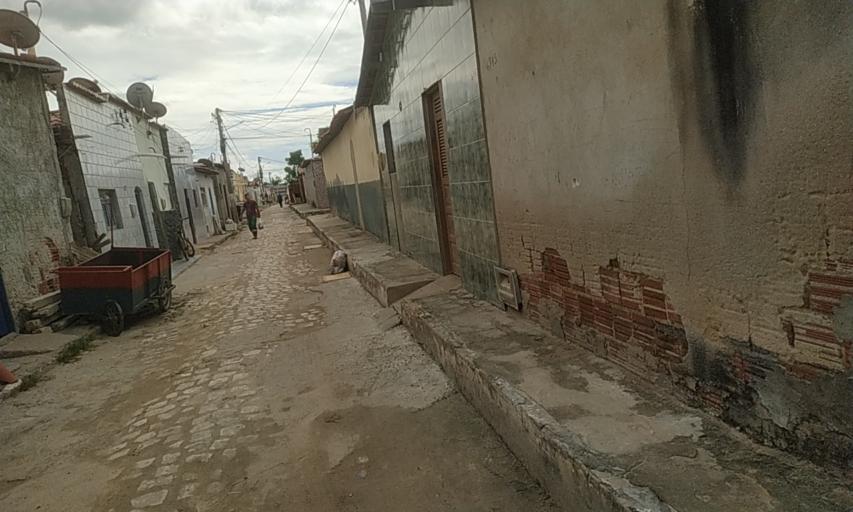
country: BR
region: Rio Grande do Norte
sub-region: Areia Branca
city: Areia Branca
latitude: -4.9557
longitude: -37.1276
